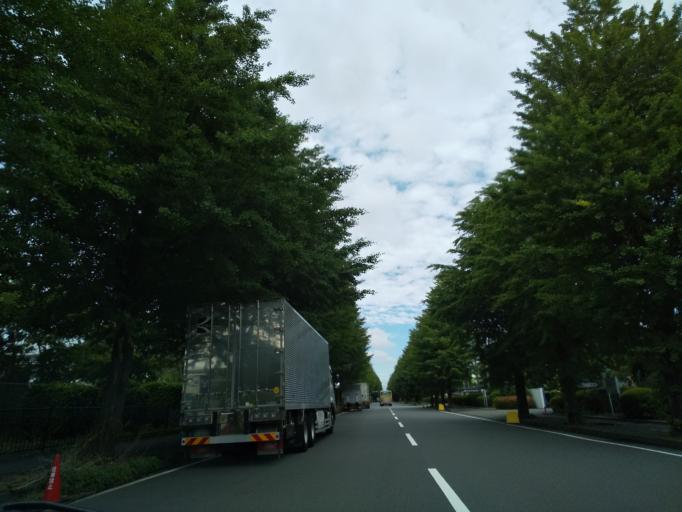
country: JP
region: Kanagawa
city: Zama
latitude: 35.5120
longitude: 139.3496
